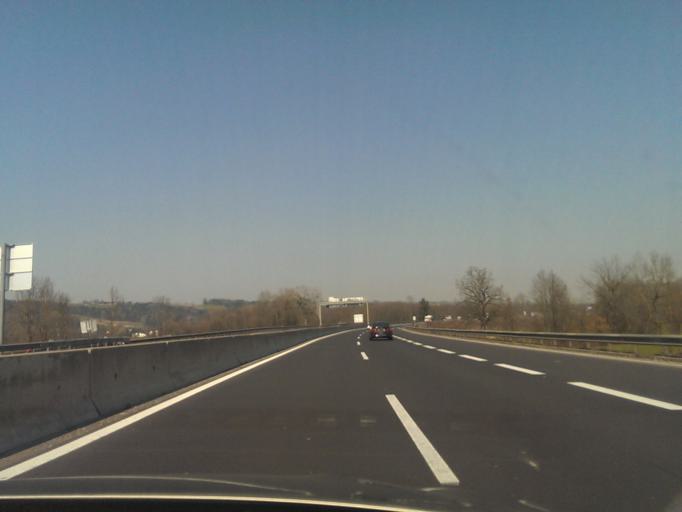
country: AT
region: Upper Austria
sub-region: Politischer Bezirk Kirchdorf an der Krems
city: Micheldorf in Oberoesterreich
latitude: 47.9315
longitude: 14.0968
